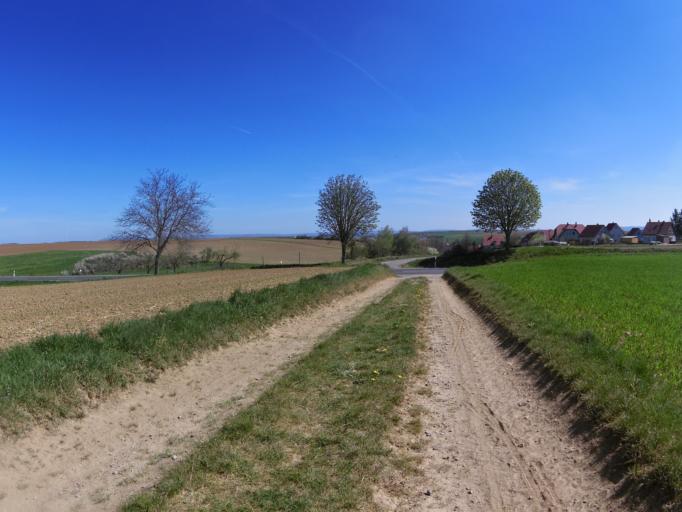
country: DE
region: Bavaria
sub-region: Regierungsbezirk Unterfranken
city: Biebelried
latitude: 49.8010
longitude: 10.1025
